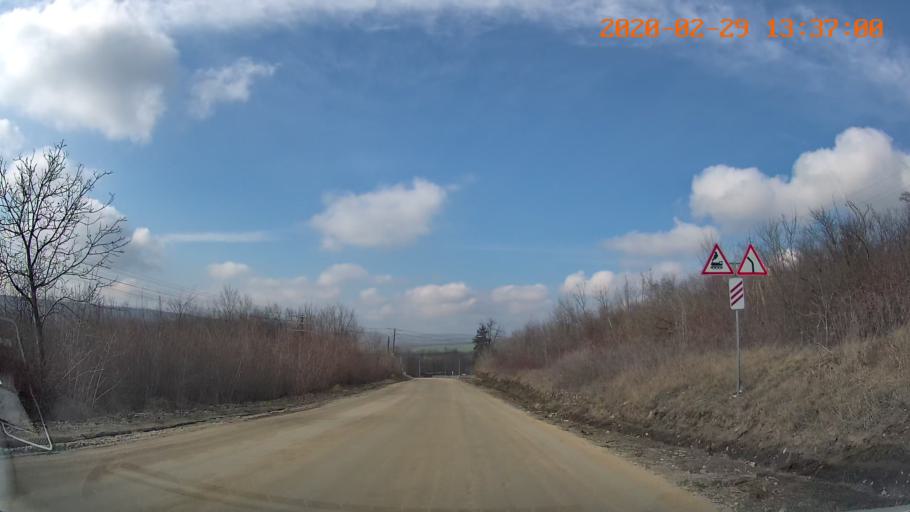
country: MD
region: Telenesti
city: Camenca
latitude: 47.8618
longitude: 28.6044
